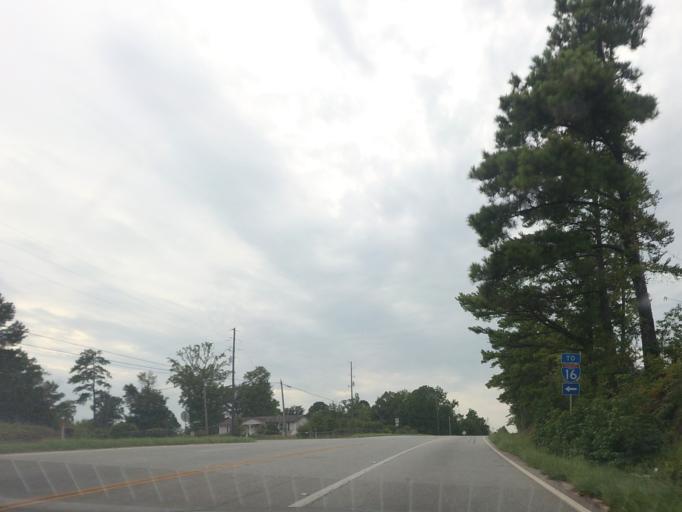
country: US
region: Georgia
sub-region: Twiggs County
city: Jeffersonville
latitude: 32.7665
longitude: -83.4809
